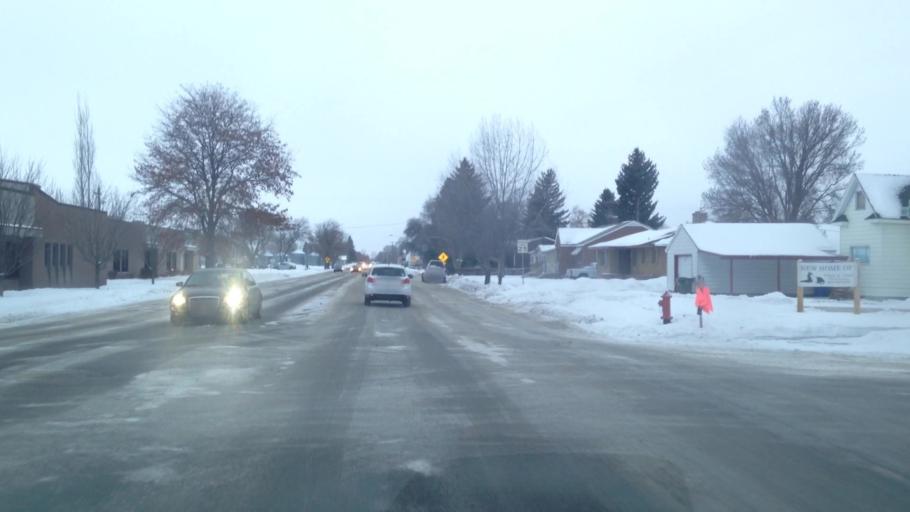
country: US
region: Idaho
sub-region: Madison County
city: Rexburg
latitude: 43.8282
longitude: -111.7837
